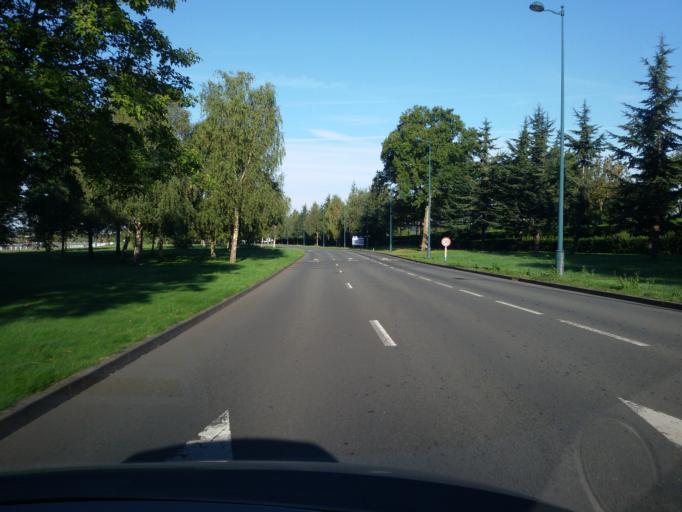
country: FR
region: Ile-de-France
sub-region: Departement de Seine-et-Marne
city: Coupvray
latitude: 48.8782
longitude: 2.7931
